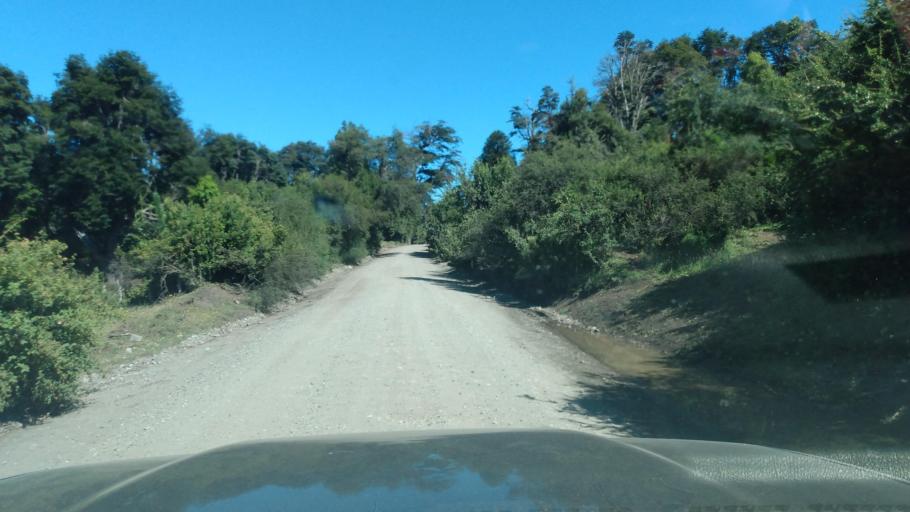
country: AR
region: Neuquen
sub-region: Departamento de Lacar
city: San Martin de los Andes
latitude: -39.7543
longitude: -71.4497
